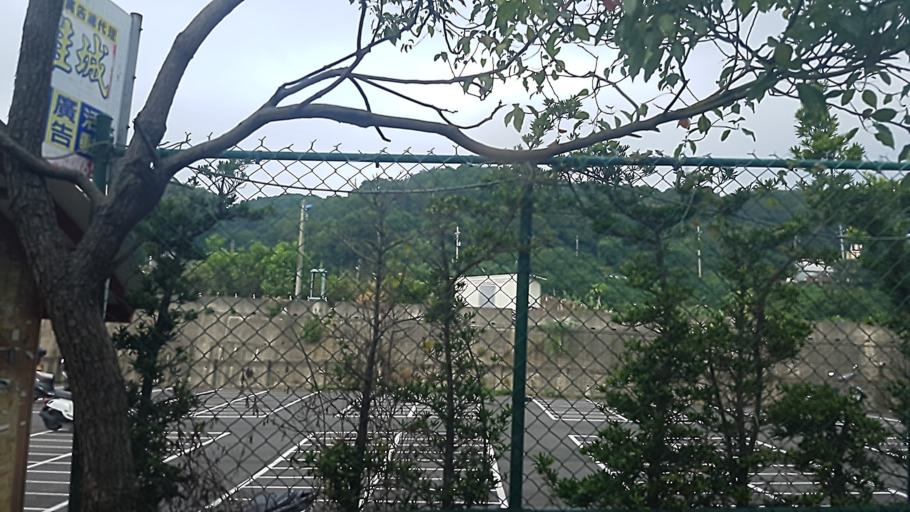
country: TW
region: Taiwan
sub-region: Hsinchu
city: Hsinchu
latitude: 24.7780
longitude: 120.9406
